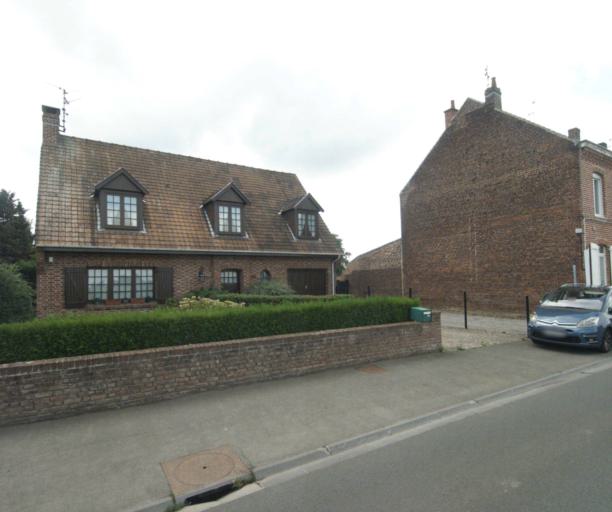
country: FR
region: Nord-Pas-de-Calais
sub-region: Departement du Nord
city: Faches-Thumesnil
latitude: 50.5946
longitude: 3.0575
